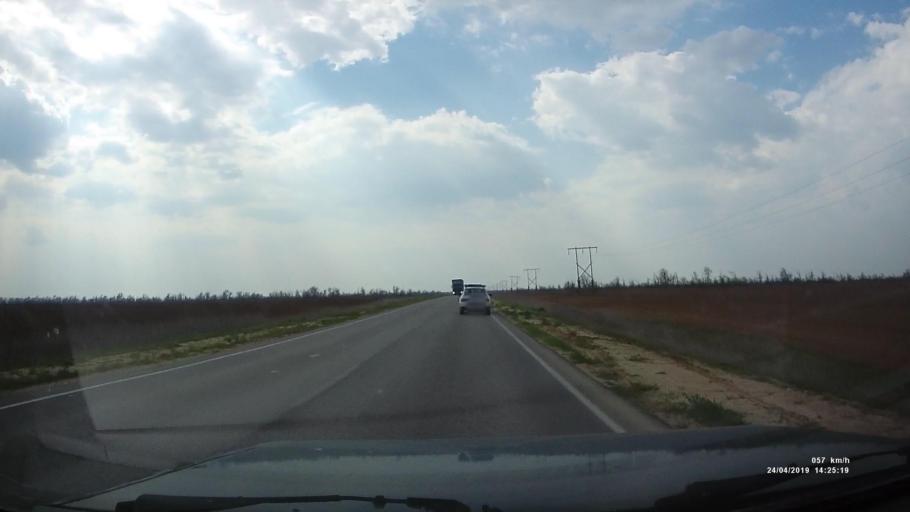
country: RU
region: Kalmykiya
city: Arshan'
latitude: 46.3304
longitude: 44.0827
